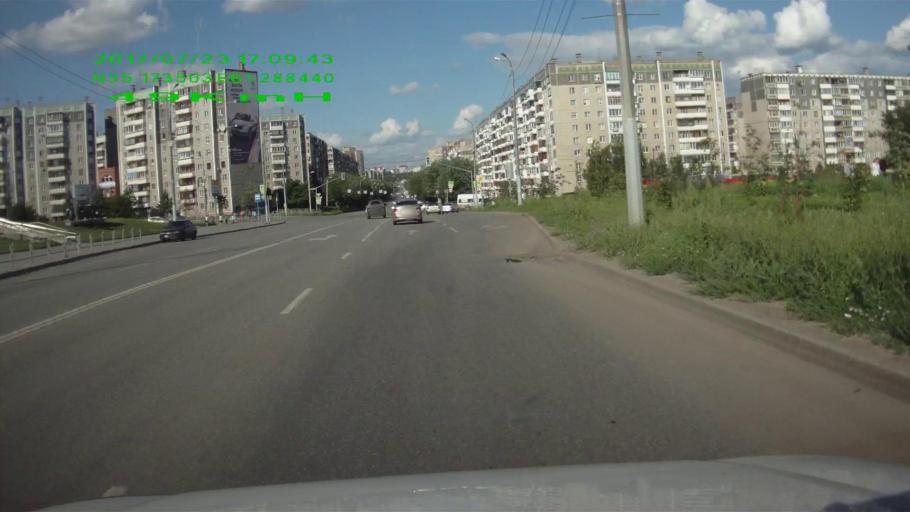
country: RU
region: Chelyabinsk
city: Roshchino
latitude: 55.1737
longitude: 61.2891
